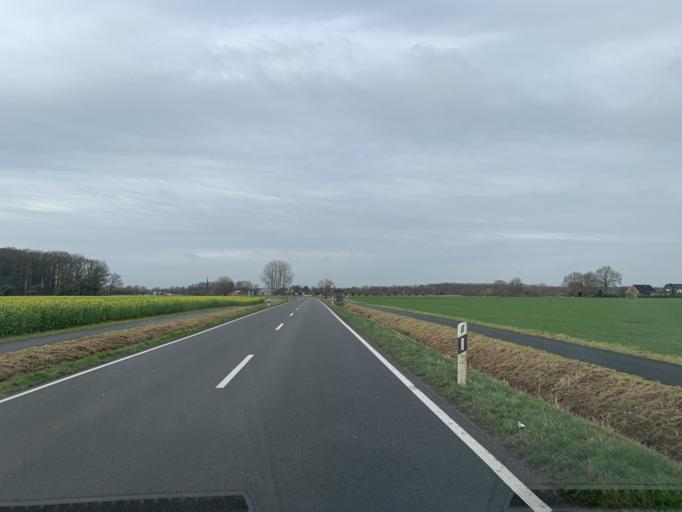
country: DE
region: North Rhine-Westphalia
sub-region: Regierungsbezirk Munster
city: Ascheberg
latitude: 51.8256
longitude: 7.5668
